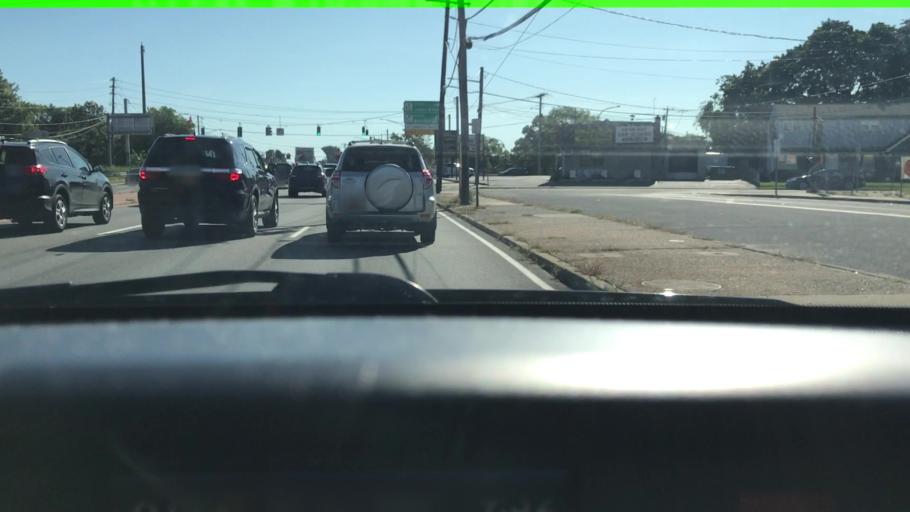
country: US
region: New York
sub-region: Nassau County
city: East Meadow
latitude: 40.7241
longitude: -73.5398
